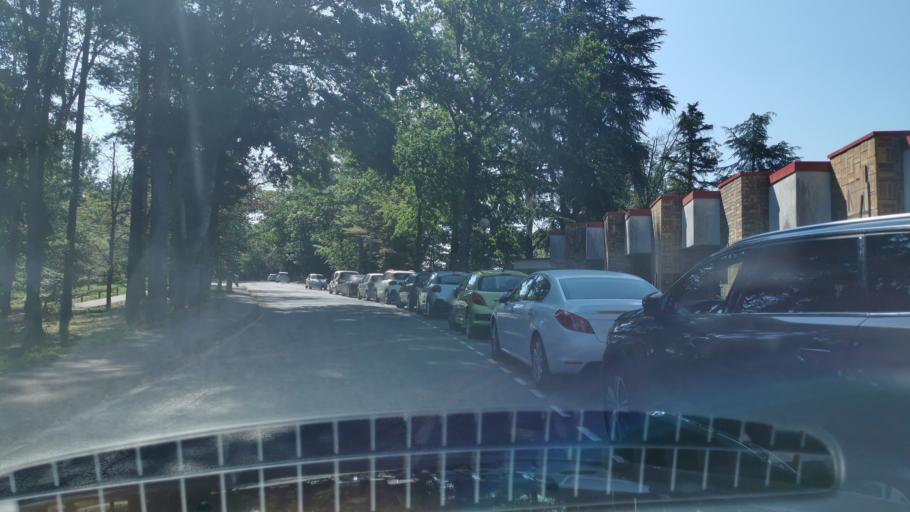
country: FR
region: Bourgogne
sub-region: Departement de Saone-et-Loire
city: Le Creusot
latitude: 46.8014
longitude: 4.4207
